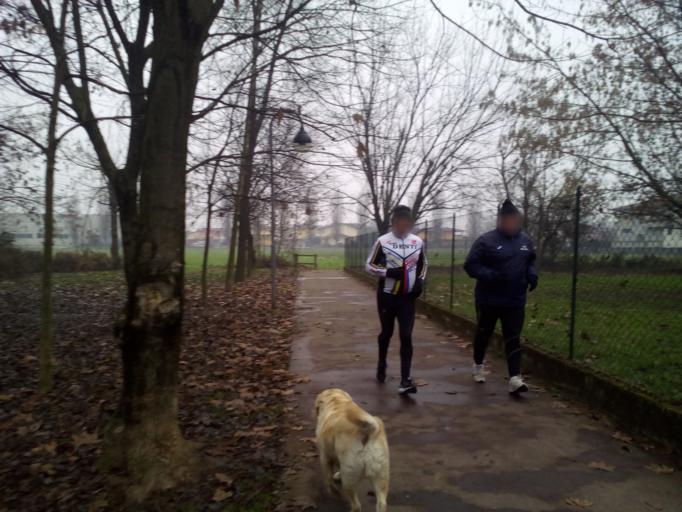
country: IT
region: Lombardy
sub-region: Provincia di Brescia
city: Castel Mella
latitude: 45.5128
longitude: 10.1447
